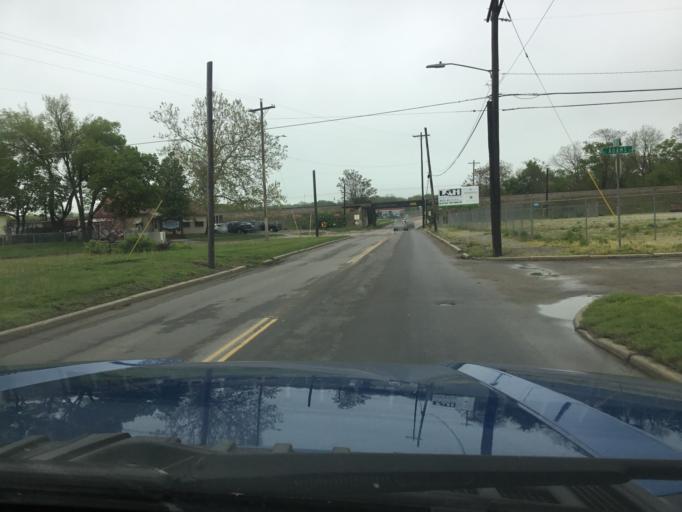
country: US
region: Kansas
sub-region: Shawnee County
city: Topeka
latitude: 39.0370
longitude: -95.6722
